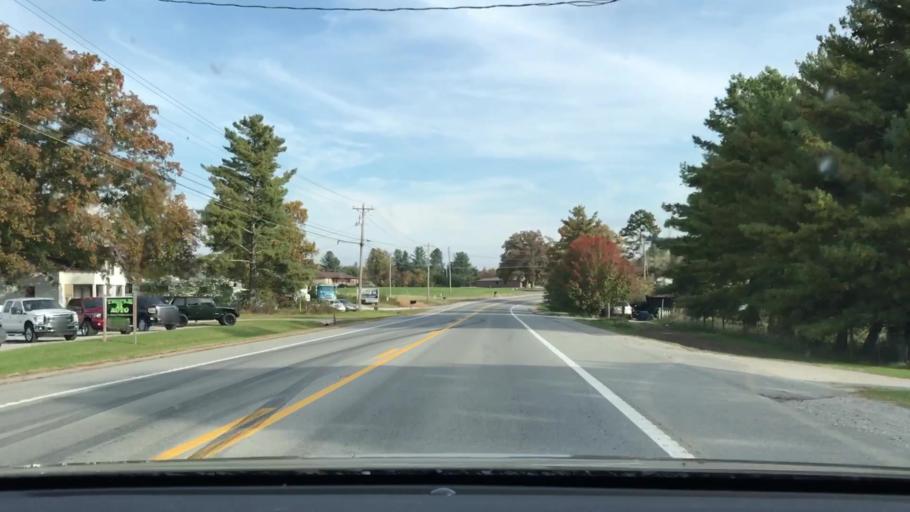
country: US
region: Tennessee
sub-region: Fentress County
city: Grimsley
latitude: 36.2637
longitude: -84.9863
